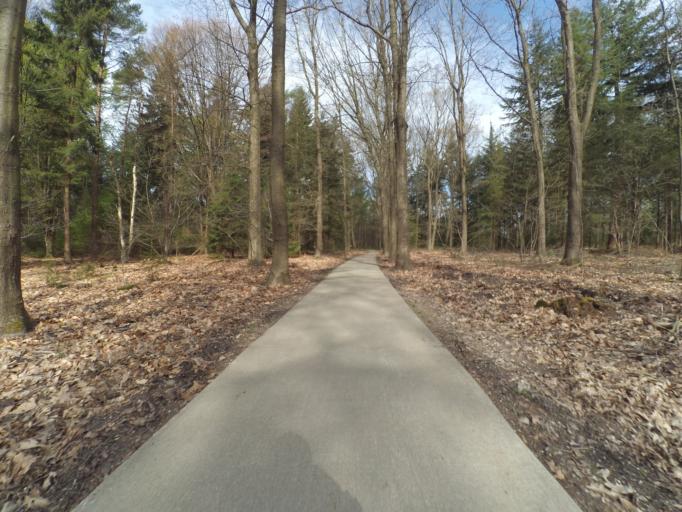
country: NL
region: Gelderland
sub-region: Gemeente Nunspeet
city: Nunspeet
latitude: 52.3368
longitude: 5.8119
